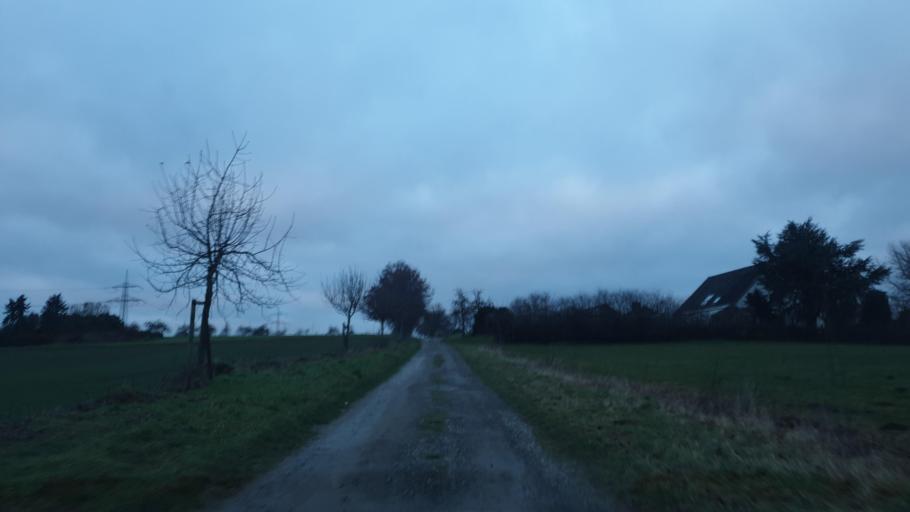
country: DE
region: North Rhine-Westphalia
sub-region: Regierungsbezirk Detmold
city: Hiddenhausen
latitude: 52.1432
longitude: 8.6324
